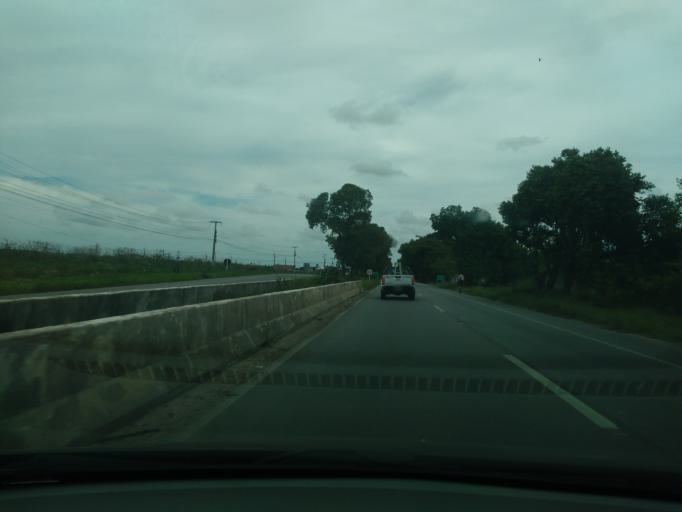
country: BR
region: Alagoas
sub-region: Rio Largo
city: Rio Largo
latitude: -9.4853
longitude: -35.8175
